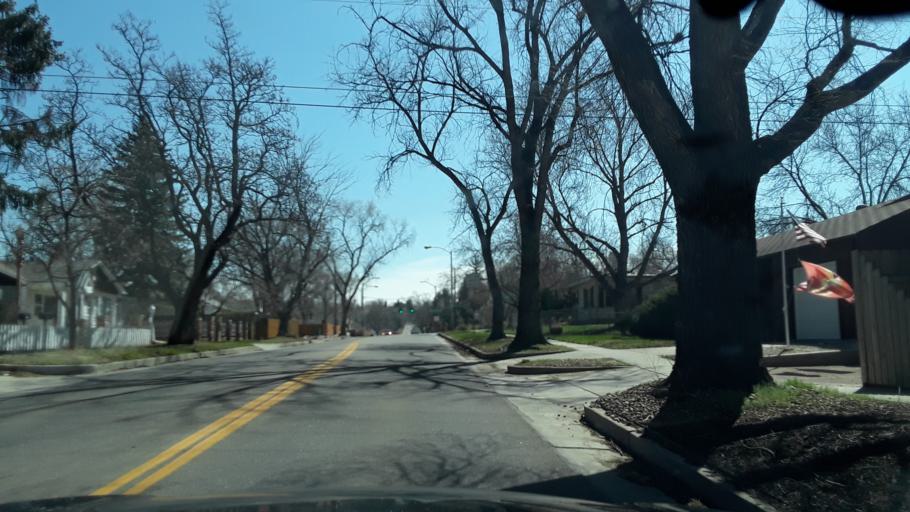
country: US
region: Colorado
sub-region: El Paso County
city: Colorado Springs
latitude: 38.8500
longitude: -104.8023
